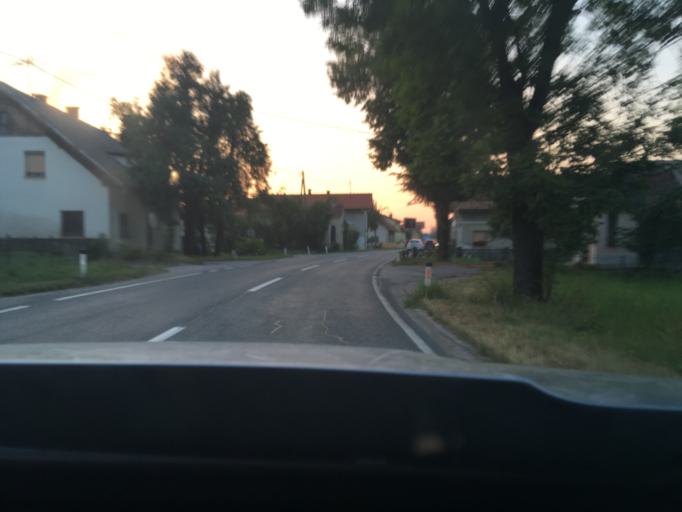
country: SI
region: Ribnica
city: Ribnica
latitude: 45.7218
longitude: 14.7426
